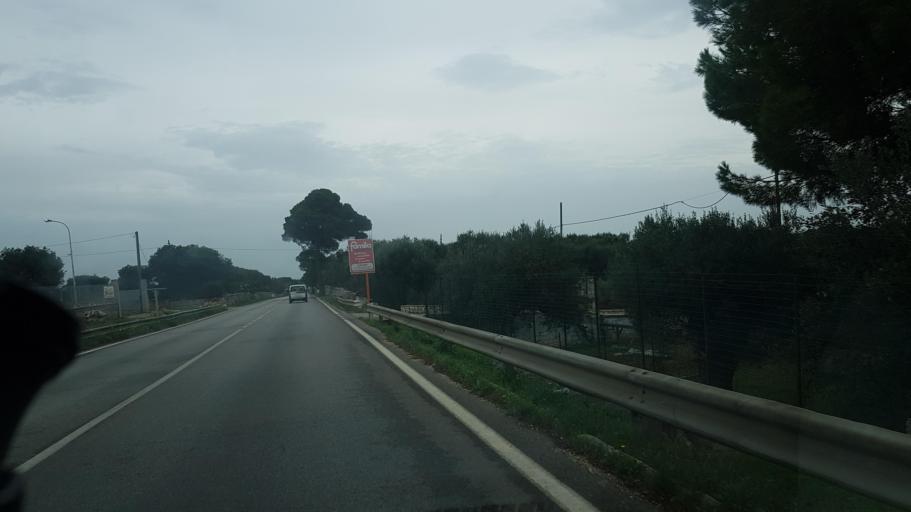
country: IT
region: Apulia
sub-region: Provincia di Brindisi
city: Carovigno
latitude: 40.7154
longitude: 17.6219
